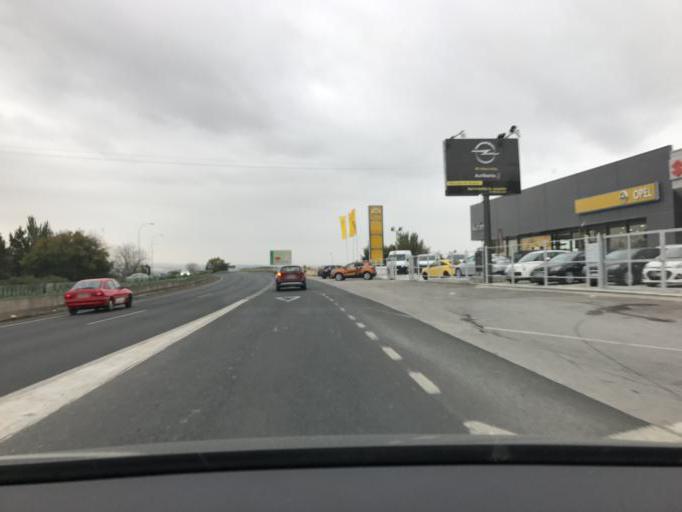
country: ES
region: Andalusia
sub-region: Provincia de Granada
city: Maracena
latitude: 37.1979
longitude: -3.6468
